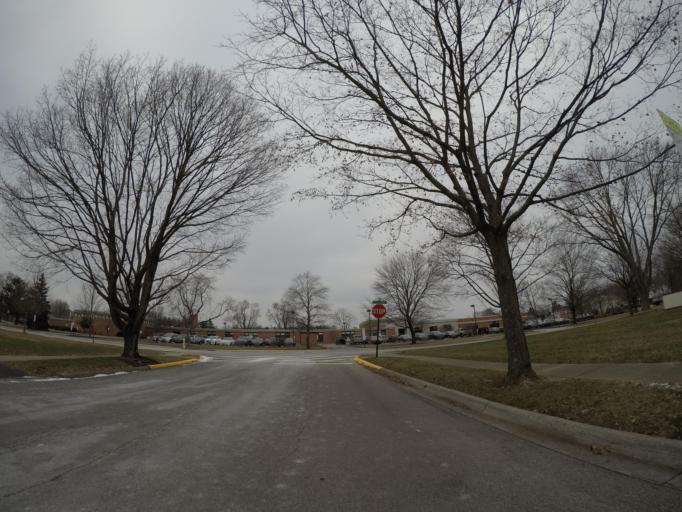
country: US
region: Ohio
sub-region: Franklin County
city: Upper Arlington
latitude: 40.0459
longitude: -83.0576
